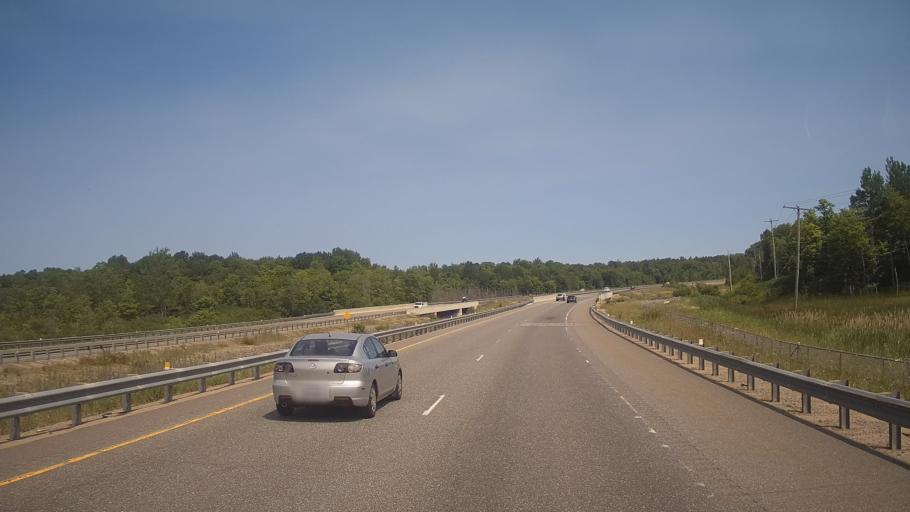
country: CA
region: Ontario
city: Midland
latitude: 45.0202
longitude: -79.7781
